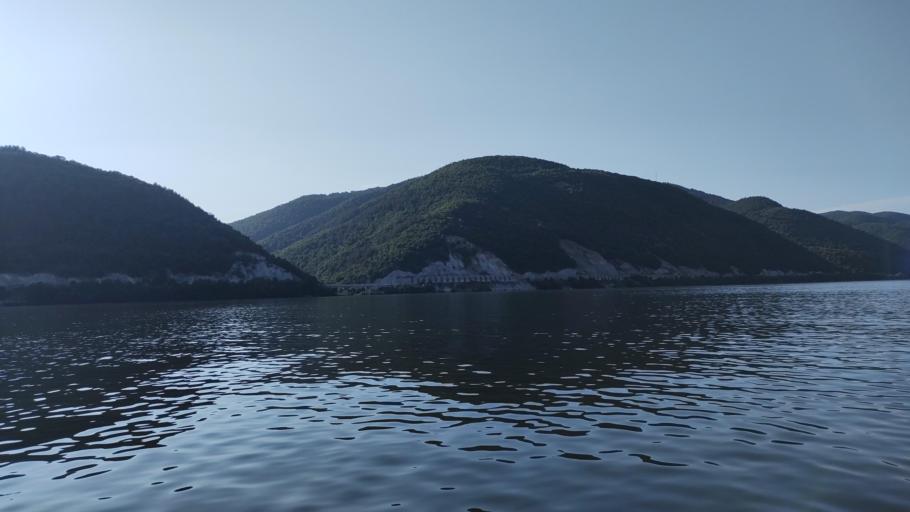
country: RO
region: Mehedinti
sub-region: Comuna Dubova
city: Dubova
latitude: 44.5378
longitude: 22.2175
